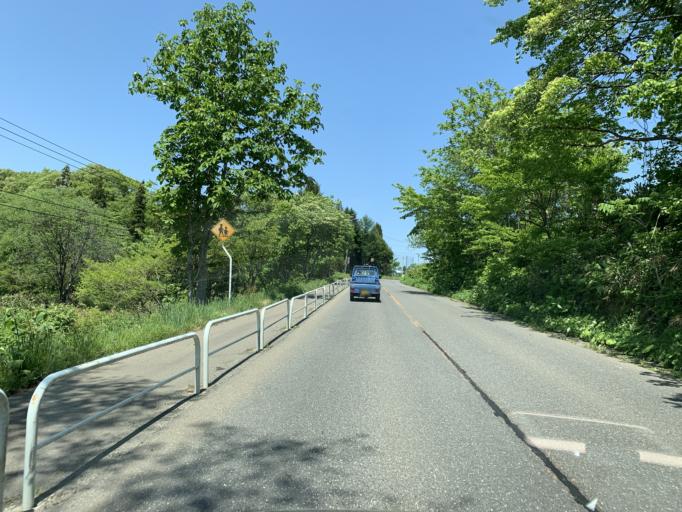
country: JP
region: Akita
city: Kakunodatemachi
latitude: 39.4515
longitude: 140.7656
